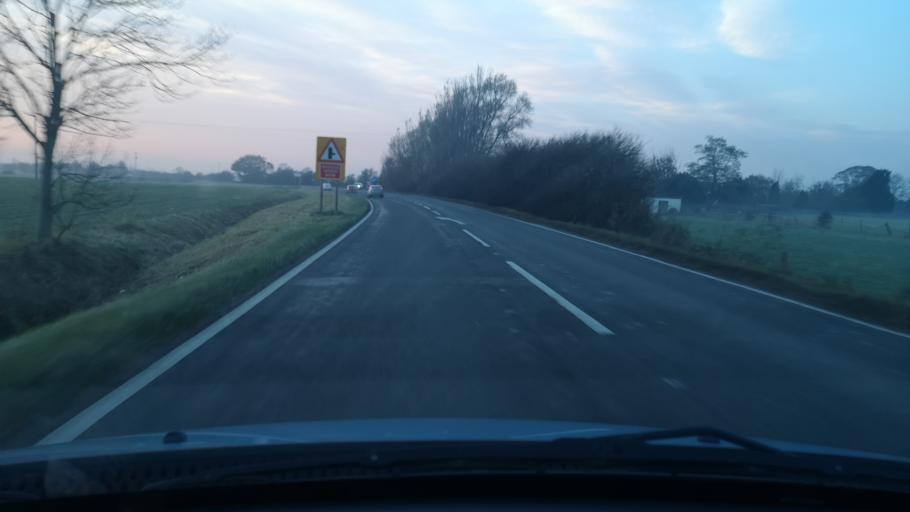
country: GB
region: England
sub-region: Doncaster
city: Hatfield
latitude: 53.5932
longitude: -0.9447
